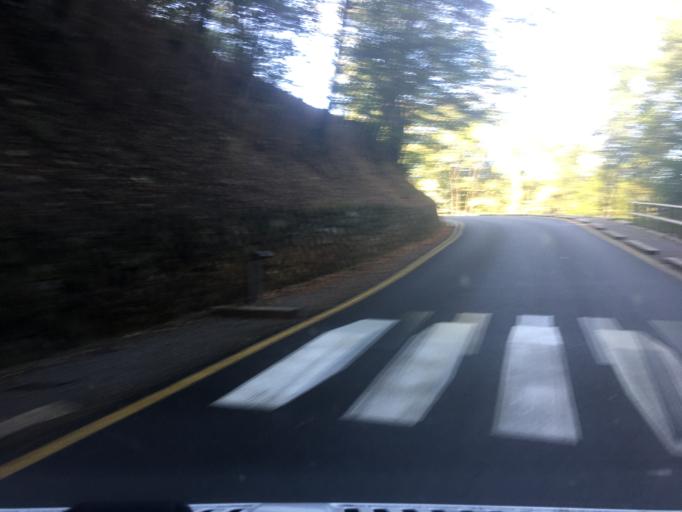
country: FR
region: Auvergne
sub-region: Departement du Cantal
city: Lanobre
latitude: 45.4440
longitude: 2.5077
